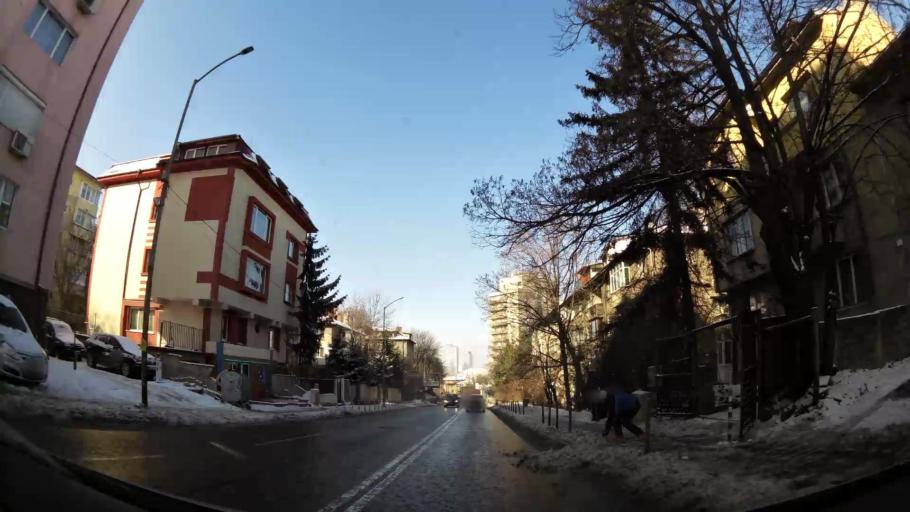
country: BG
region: Sofia-Capital
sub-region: Stolichna Obshtina
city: Sofia
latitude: 42.6773
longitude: 23.3318
